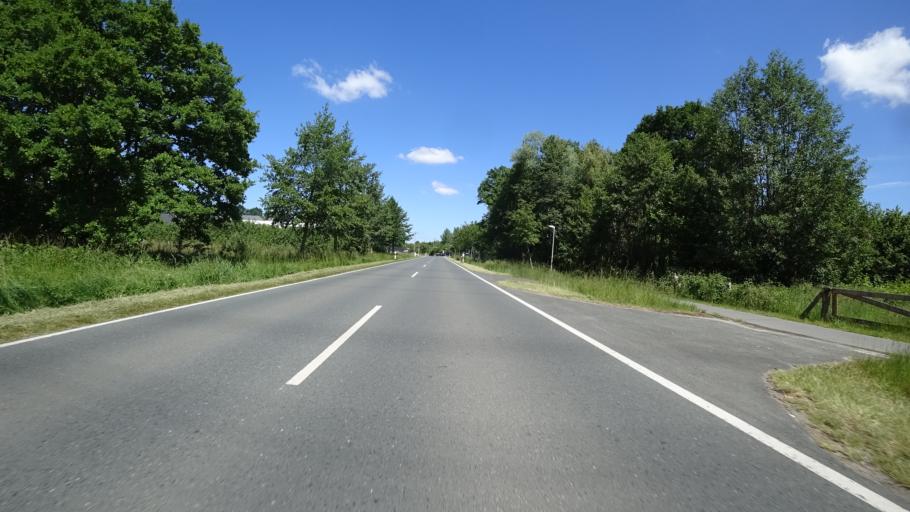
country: DE
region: North Rhine-Westphalia
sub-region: Regierungsbezirk Detmold
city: Guetersloh
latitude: 51.9285
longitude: 8.4264
